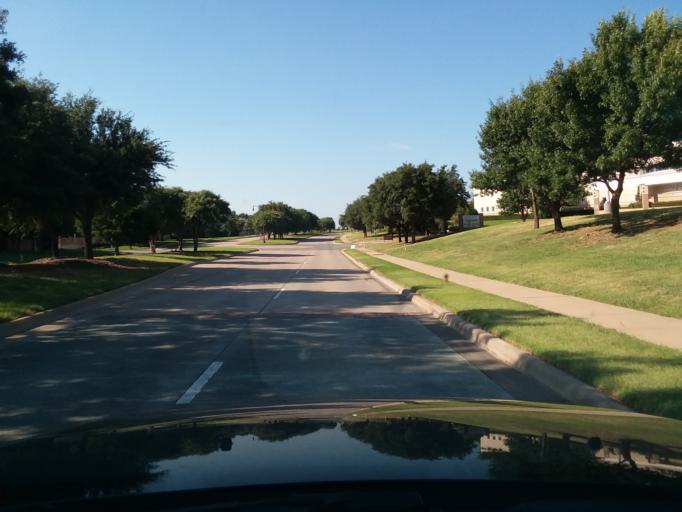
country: US
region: Texas
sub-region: Denton County
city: Double Oak
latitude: 33.0622
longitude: -97.0941
